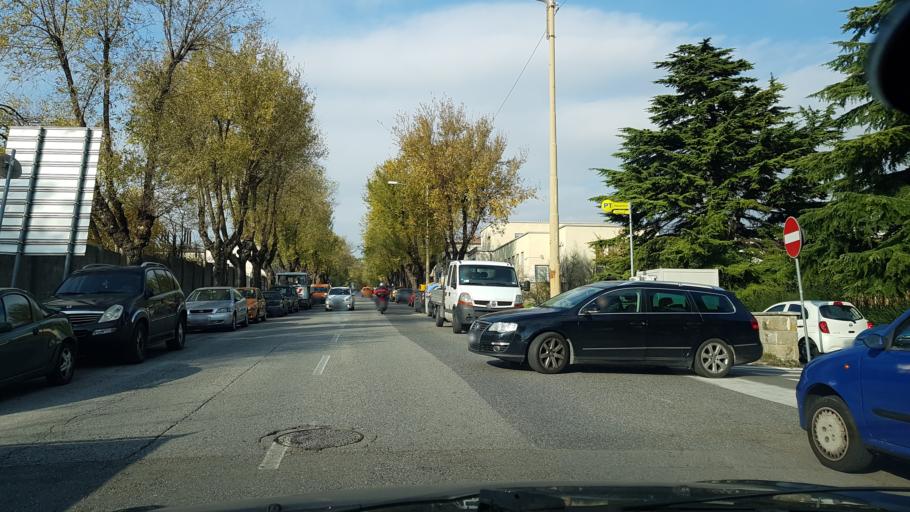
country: IT
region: Friuli Venezia Giulia
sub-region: Provincia di Trieste
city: Trieste
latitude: 45.6180
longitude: 13.8032
